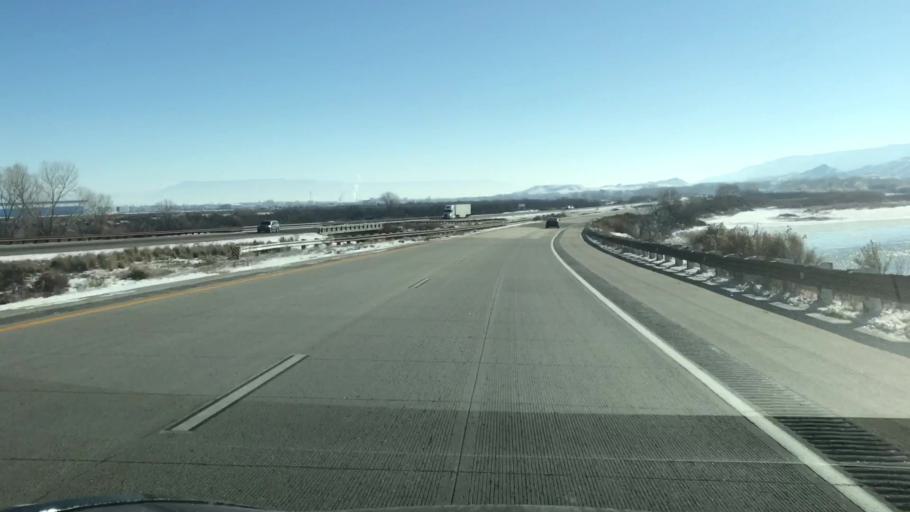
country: US
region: Colorado
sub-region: Mesa County
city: Loma
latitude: 39.1761
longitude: -108.8019
